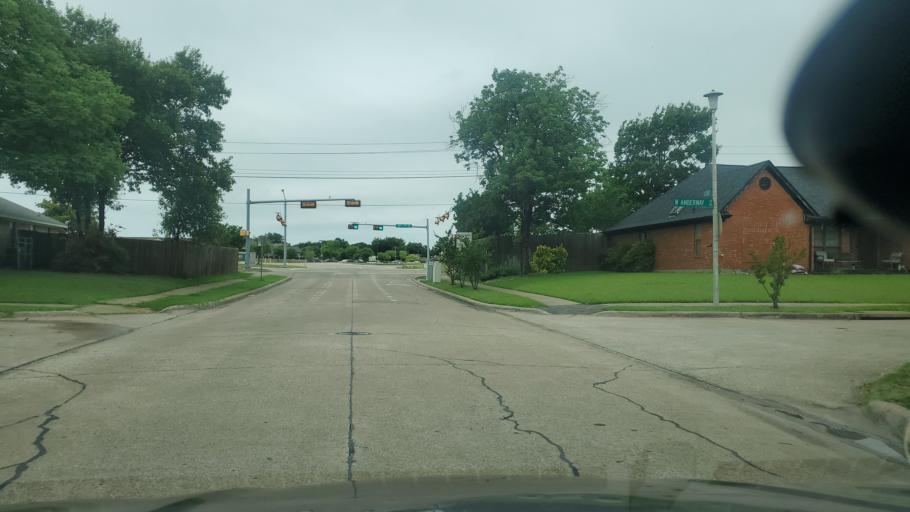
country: US
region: Texas
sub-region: Dallas County
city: Garland
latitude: 32.9379
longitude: -96.6328
